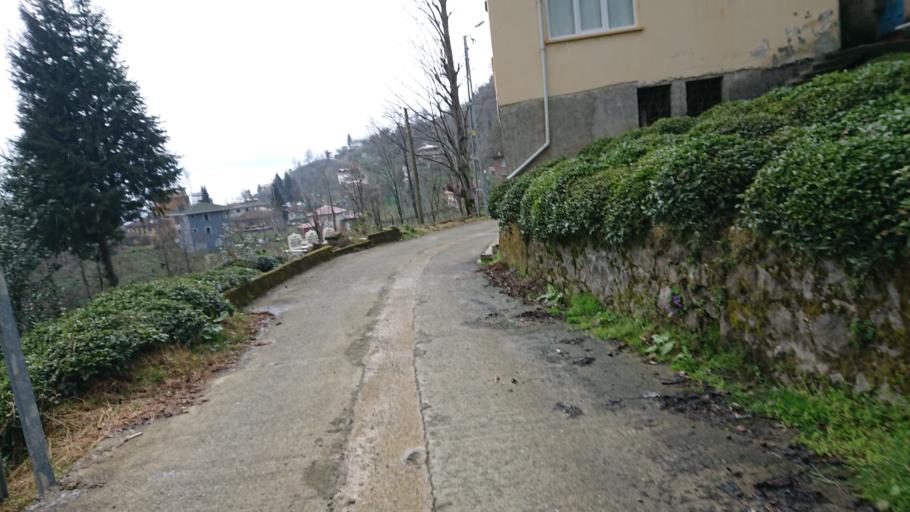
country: TR
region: Rize
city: Rize
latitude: 40.9798
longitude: 40.4961
